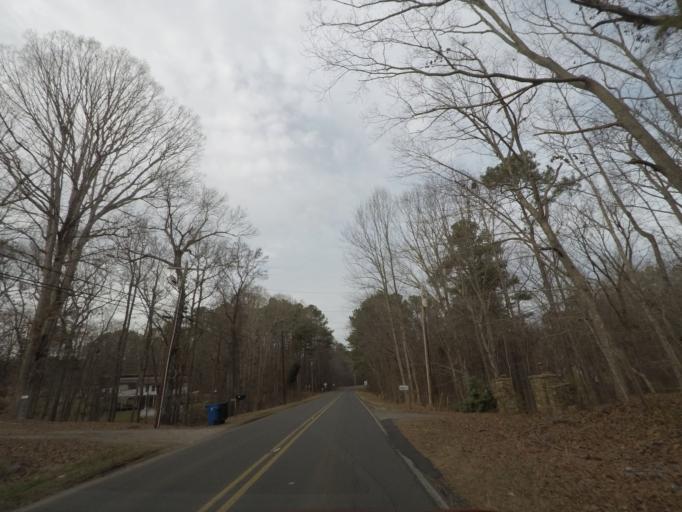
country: US
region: North Carolina
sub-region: Durham County
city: Durham
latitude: 36.0779
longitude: -78.9744
